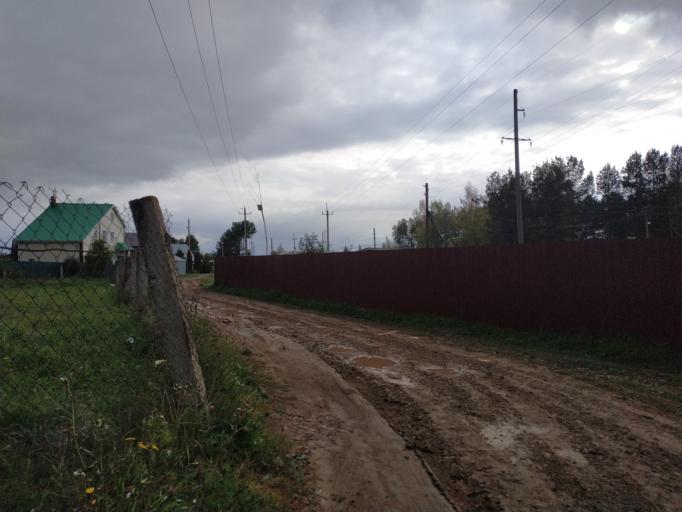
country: RU
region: Chuvashia
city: Ishley
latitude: 56.1294
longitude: 47.0912
